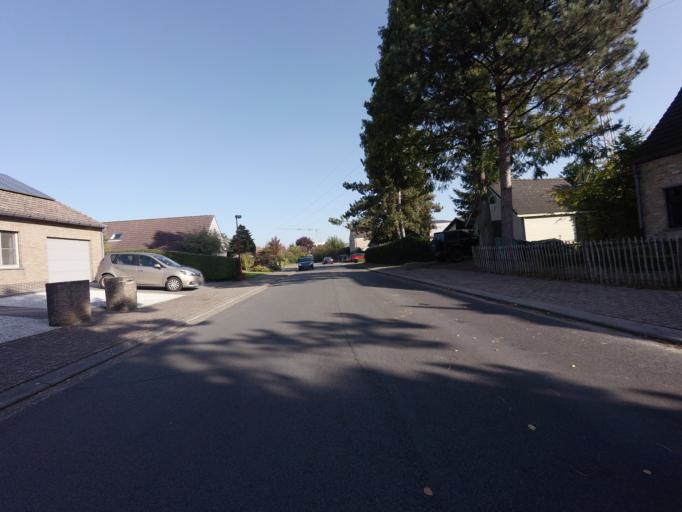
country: BE
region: Flanders
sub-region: Provincie Antwerpen
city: Lint
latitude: 51.1207
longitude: 4.4903
